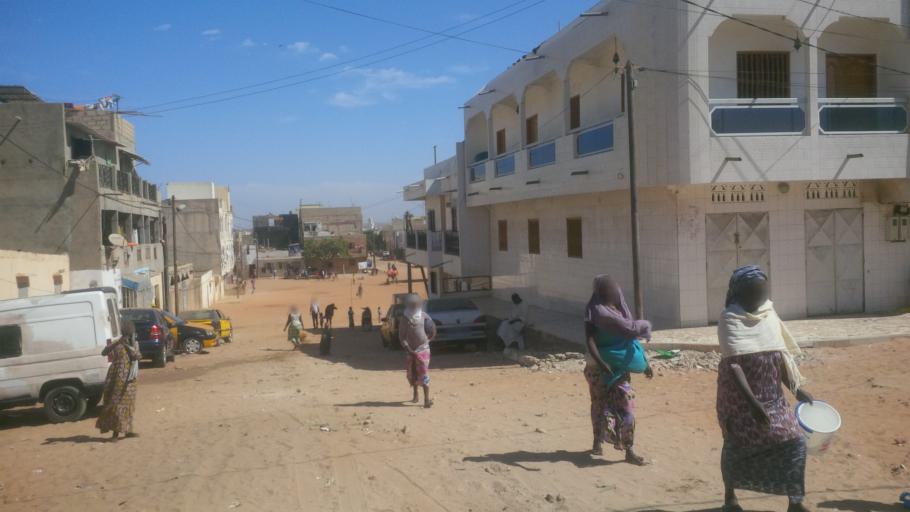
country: SN
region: Dakar
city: Pikine
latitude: 14.7810
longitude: -17.3810
